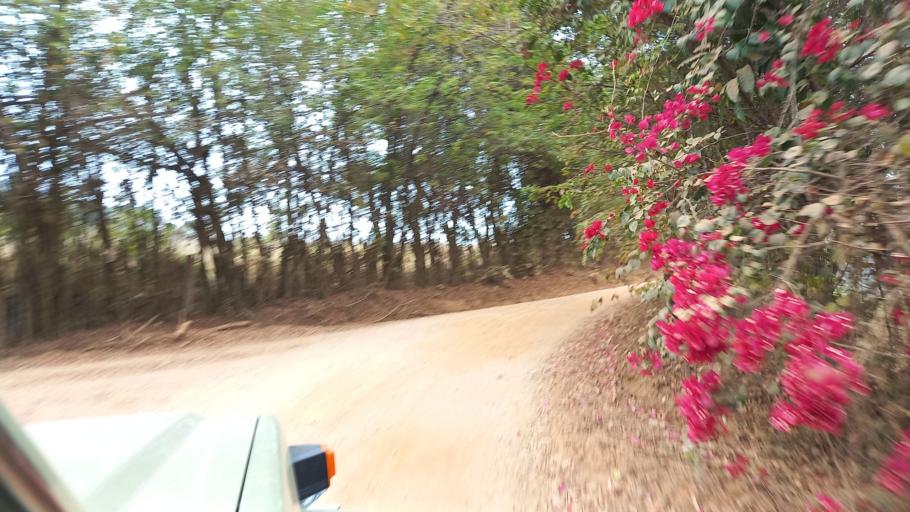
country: BR
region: Sao Paulo
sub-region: Moji-Guacu
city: Mogi-Gaucu
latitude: -22.2947
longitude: -46.8317
